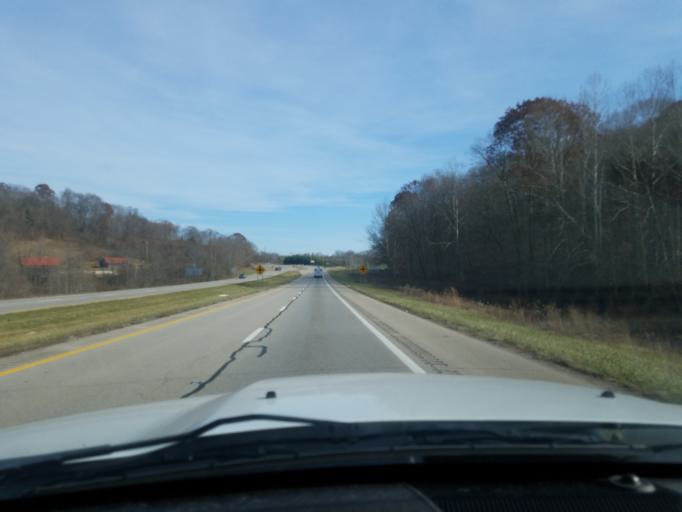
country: US
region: Ohio
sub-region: Jackson County
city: Jackson
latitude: 39.0137
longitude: -82.6506
